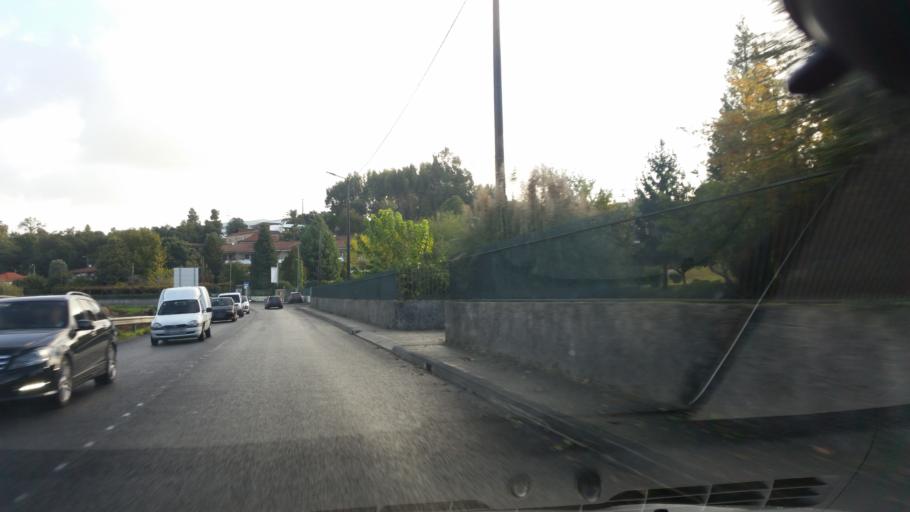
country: PT
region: Porto
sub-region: Santo Tirso
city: Sao Miguel do Couto
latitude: 41.3446
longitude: -8.4642
